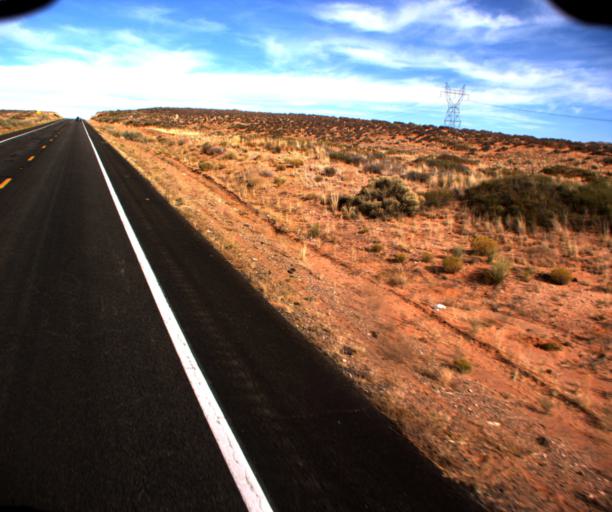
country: US
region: Arizona
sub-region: Apache County
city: Many Farms
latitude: 36.9459
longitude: -109.5310
